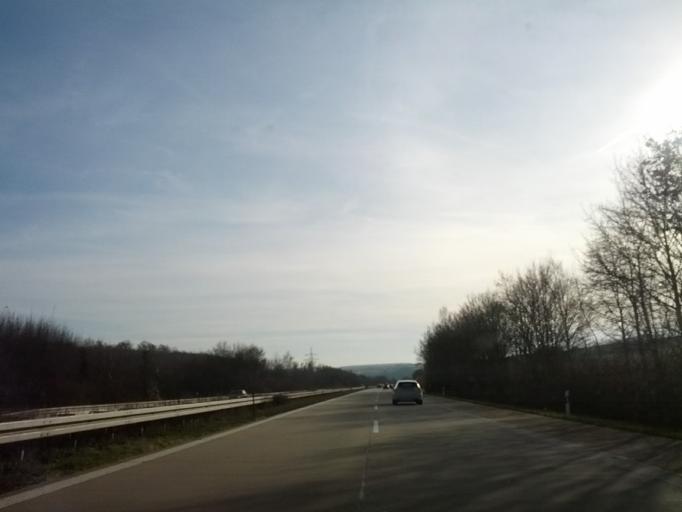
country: DE
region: Bavaria
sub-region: Regierungsbezirk Unterfranken
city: Marktsteft
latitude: 49.6872
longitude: 10.1176
